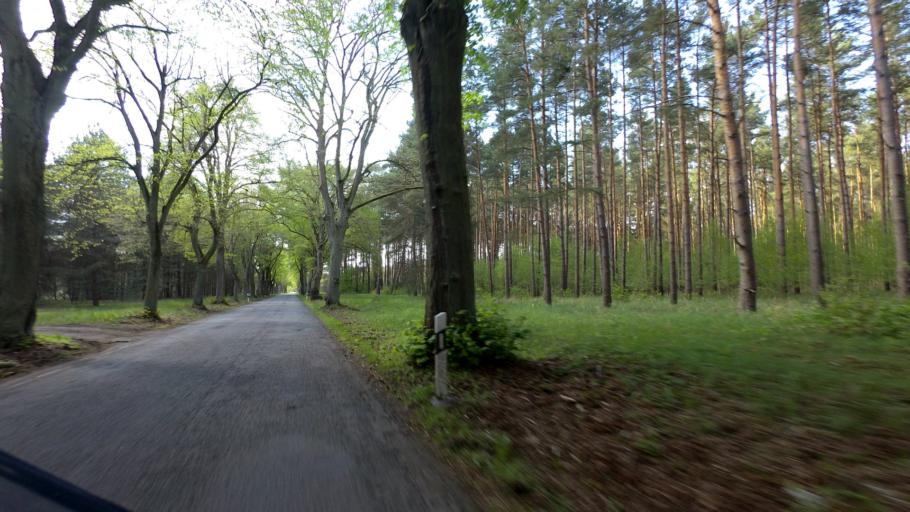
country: DE
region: Brandenburg
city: Templin
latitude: 52.9969
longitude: 13.5102
